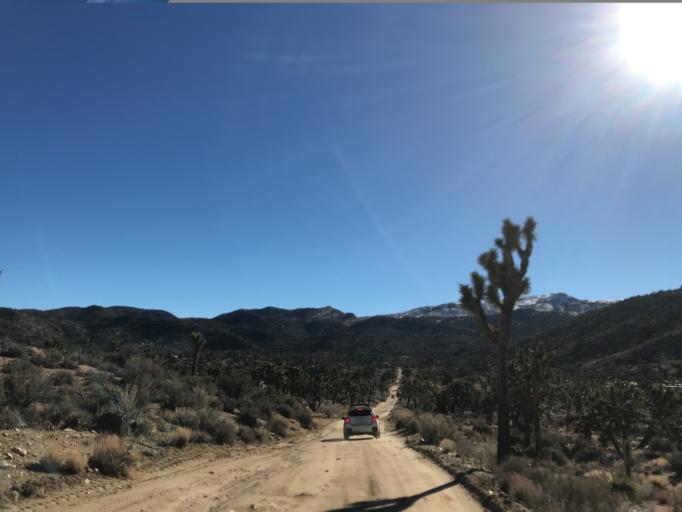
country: US
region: California
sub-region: San Bernardino County
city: Morongo Valley
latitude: 34.2310
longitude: -116.6389
